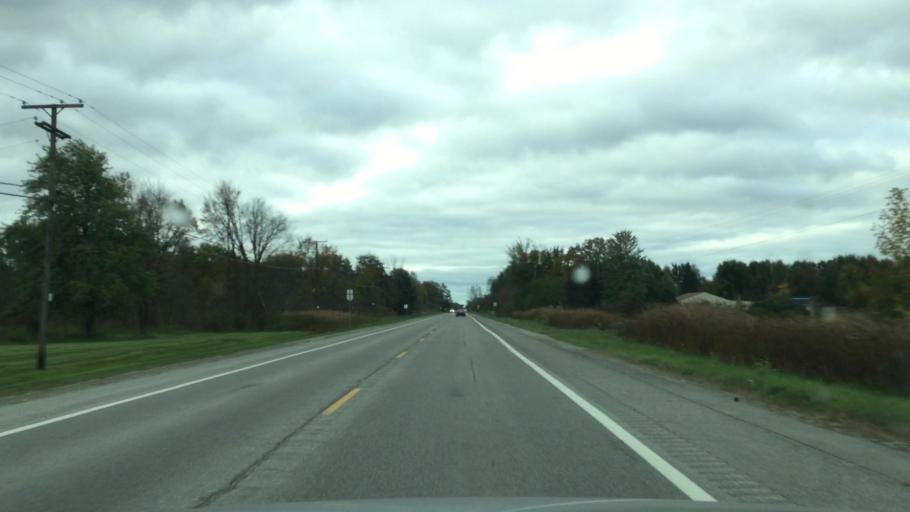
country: US
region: Michigan
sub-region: Macomb County
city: Memphis
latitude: 42.9755
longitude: -82.7644
